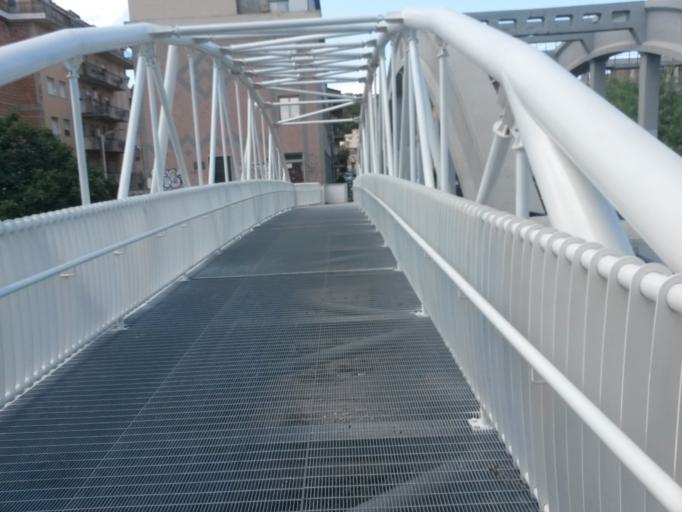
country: IT
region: Calabria
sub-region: Provincia di Catanzaro
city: Catanzaro
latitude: 38.8679
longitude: 16.6033
